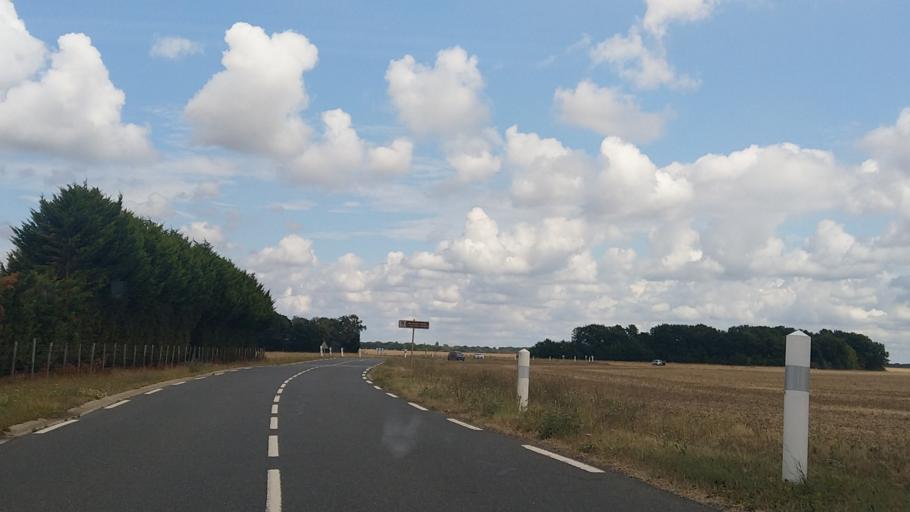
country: FR
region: Ile-de-France
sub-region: Departement des Yvelines
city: Sonchamp
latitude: 48.5798
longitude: 1.8382
